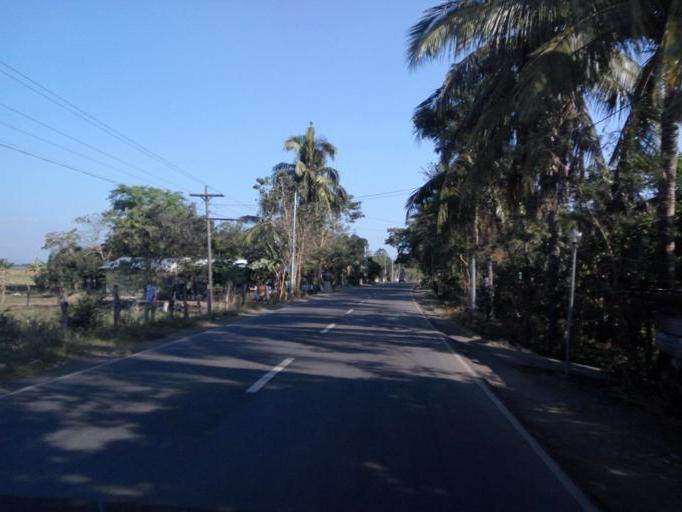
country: PH
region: Cagayan Valley
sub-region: Province of Cagayan
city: Amulung
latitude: 17.8280
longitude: 121.7247
